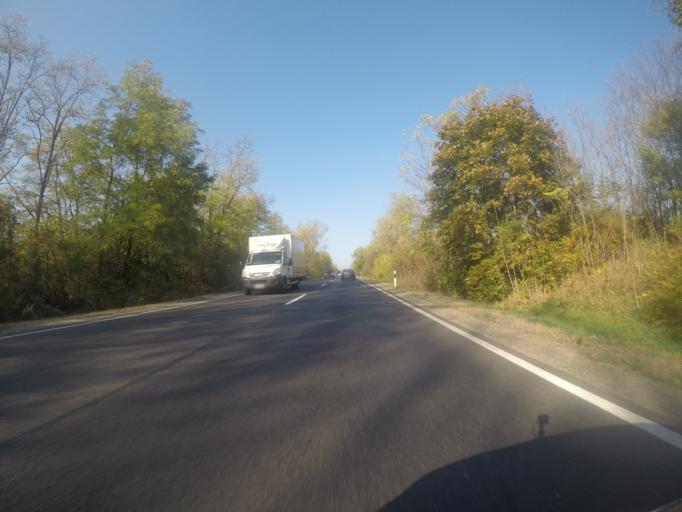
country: HU
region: Fejer
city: Baracs
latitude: 46.8766
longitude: 18.9185
